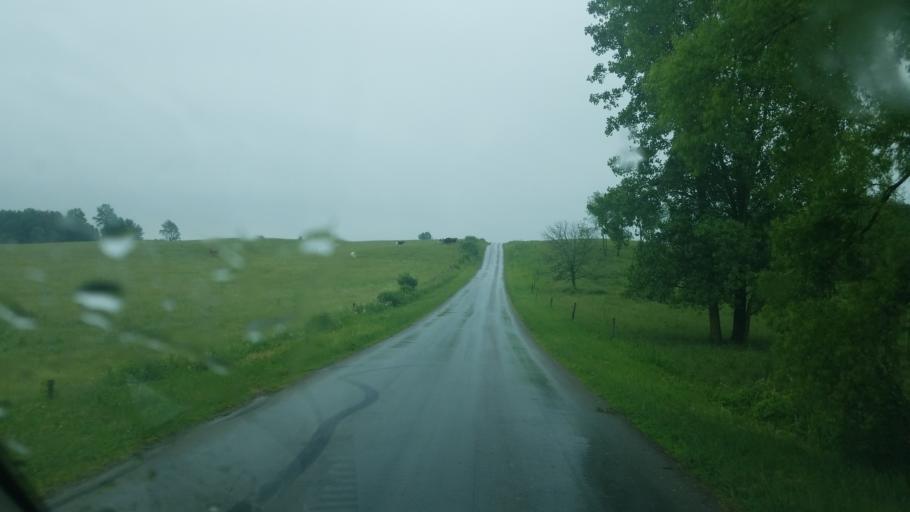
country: US
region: Ohio
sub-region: Huron County
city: Plymouth
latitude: 40.9801
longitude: -82.5908
